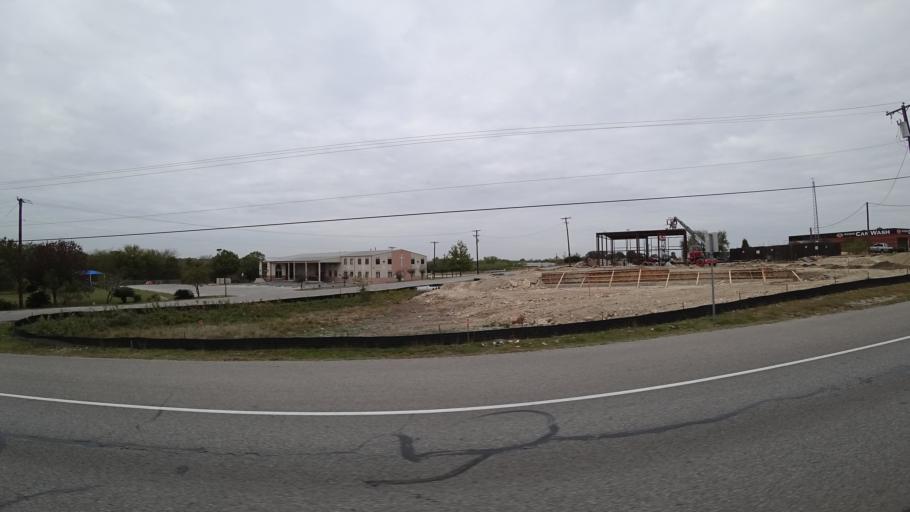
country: US
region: Texas
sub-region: Travis County
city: Windemere
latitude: 30.4471
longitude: -97.6415
